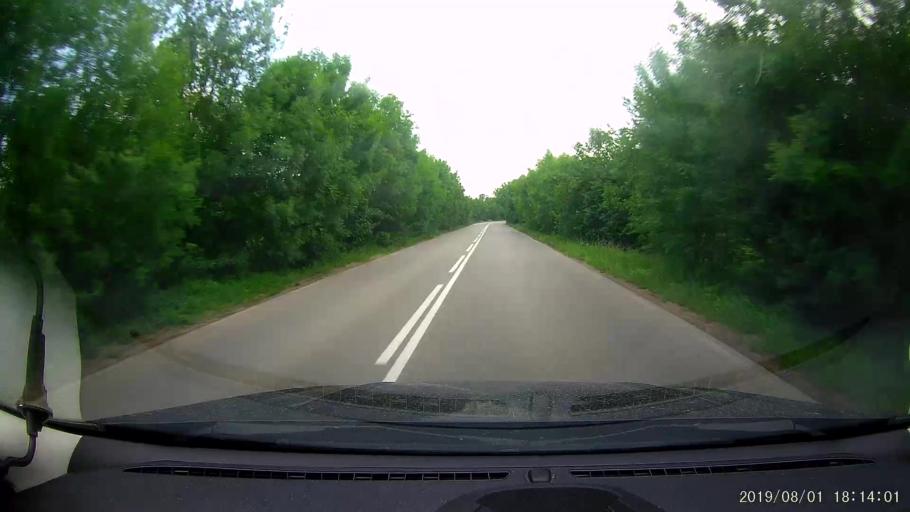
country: BG
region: Silistra
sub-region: Obshtina Dulovo
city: Dulovo
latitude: 43.7772
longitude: 27.1296
